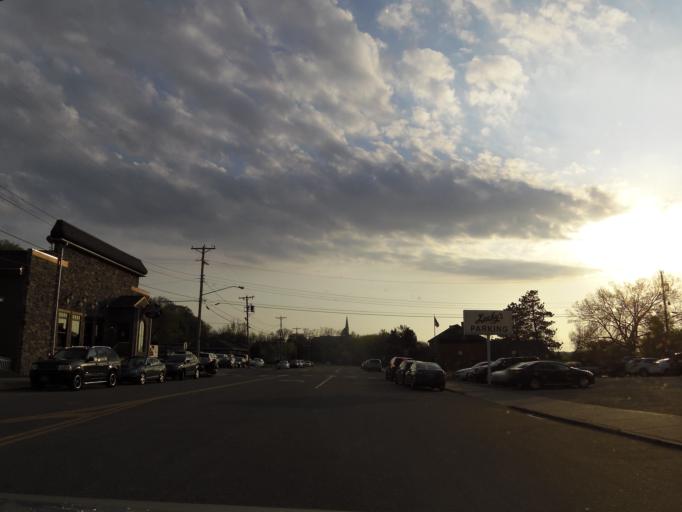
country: US
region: Minnesota
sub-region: Dakota County
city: Mendota Heights
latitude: 44.8879
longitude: -93.1635
